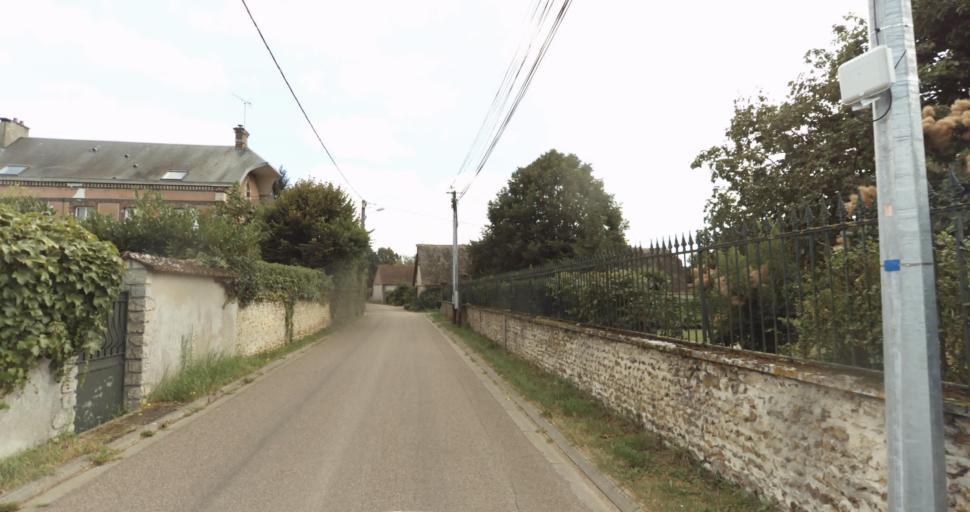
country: FR
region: Haute-Normandie
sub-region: Departement de l'Eure
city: La Madeleine-de-Nonancourt
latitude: 48.8307
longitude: 1.1744
